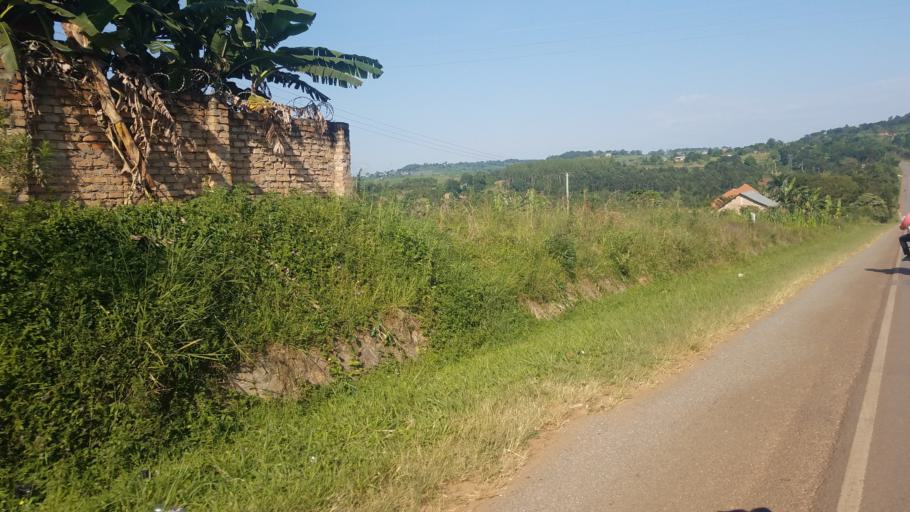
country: UG
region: Central Region
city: Masaka
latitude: -0.3370
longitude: 31.6891
